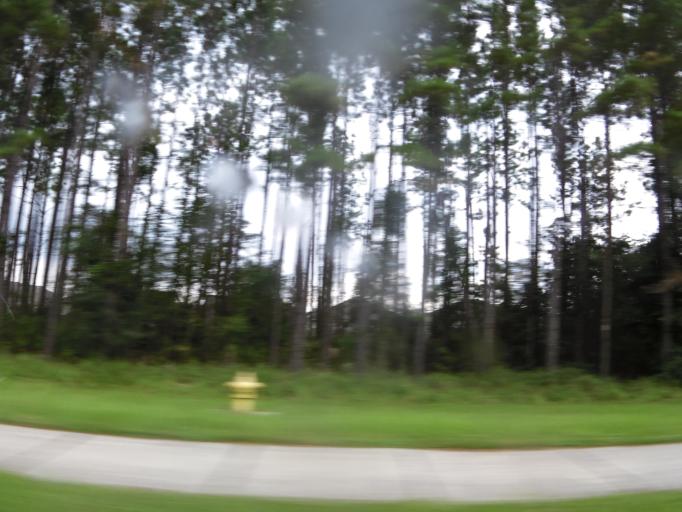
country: US
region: Florida
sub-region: Clay County
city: Lakeside
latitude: 30.1958
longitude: -81.8398
